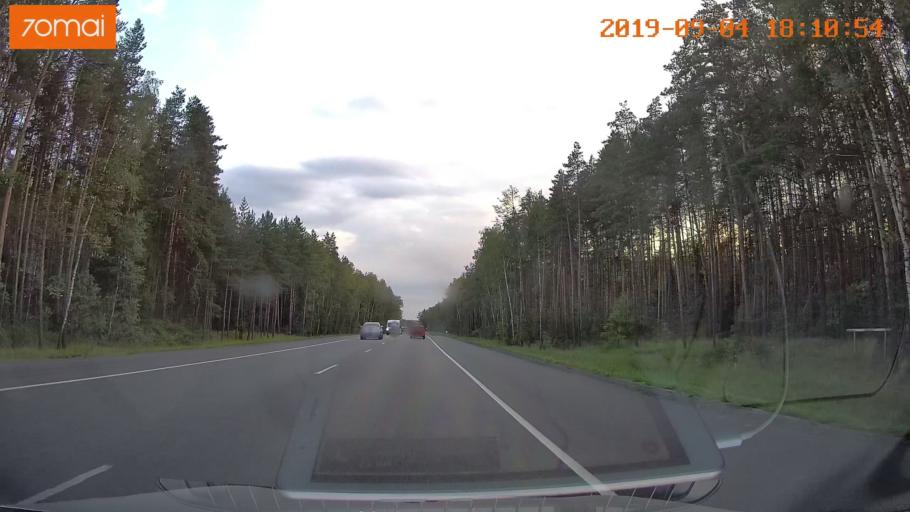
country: RU
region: Moskovskaya
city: Lopatinskiy
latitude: 55.3832
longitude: 38.7601
